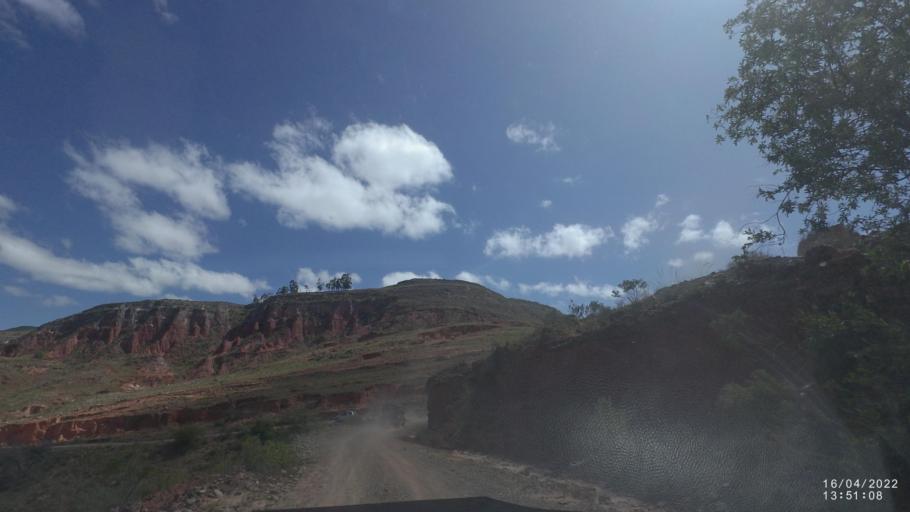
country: BO
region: Cochabamba
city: Mizque
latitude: -18.0184
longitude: -65.5743
